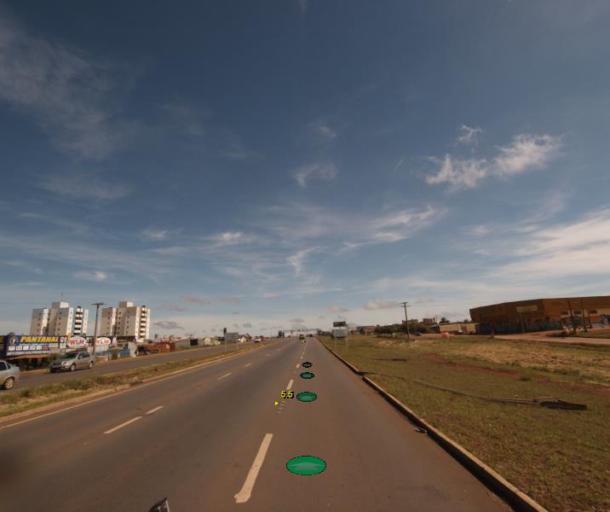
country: BR
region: Federal District
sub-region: Brasilia
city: Brasilia
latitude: -15.7538
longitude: -48.2580
